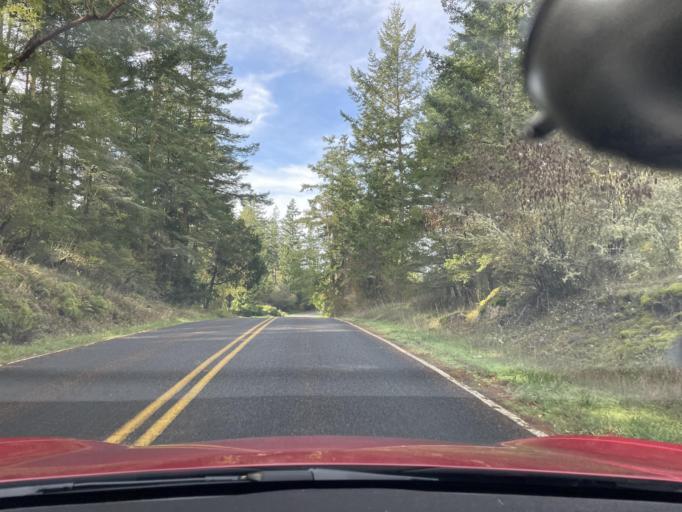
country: US
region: Washington
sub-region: San Juan County
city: Friday Harbor
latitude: 48.5259
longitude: -122.9755
